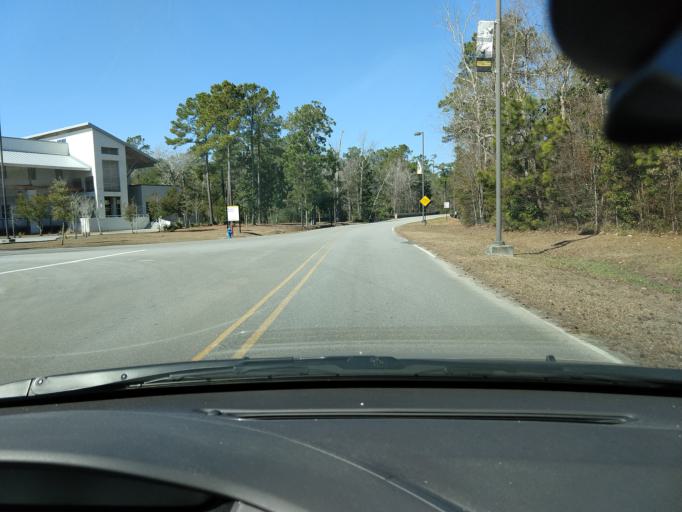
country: US
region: Mississippi
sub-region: Jackson County
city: Gulf Park Estates
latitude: 30.3939
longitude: -88.7785
